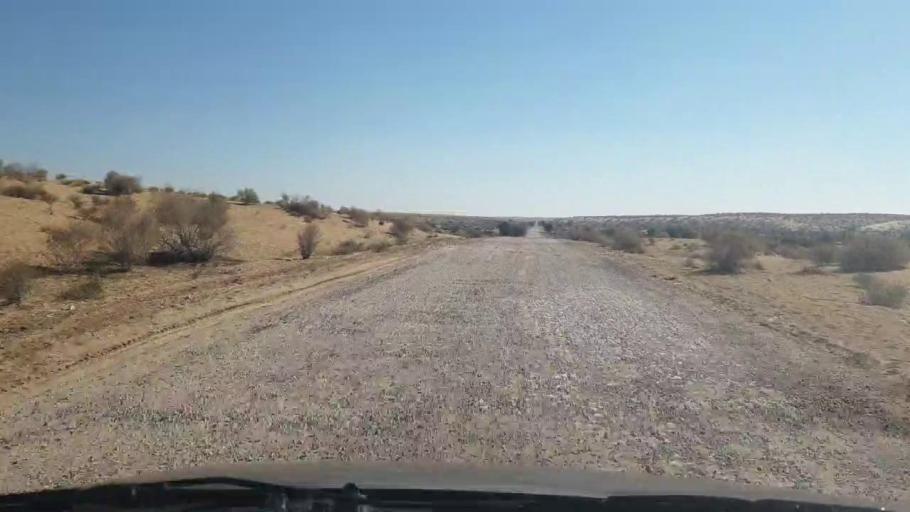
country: PK
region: Sindh
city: Bozdar
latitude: 27.0432
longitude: 68.6856
